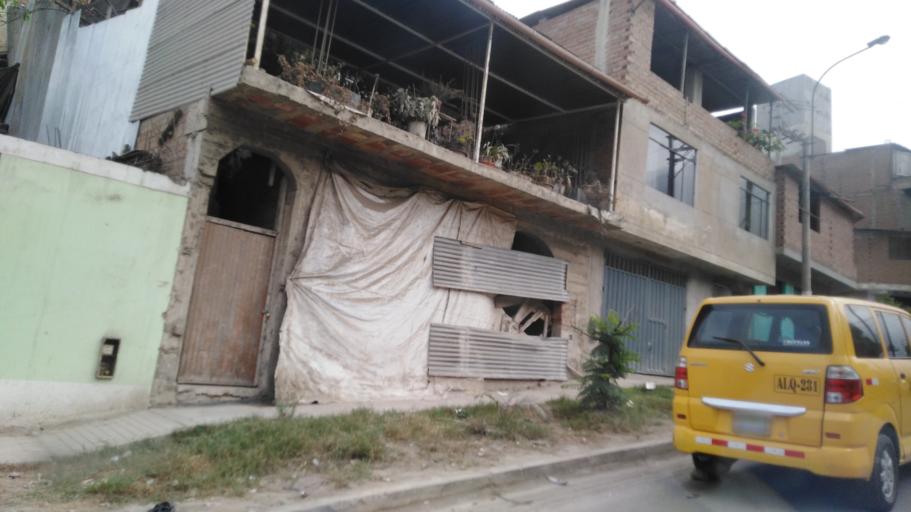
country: PE
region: Lima
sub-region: Lima
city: La Molina
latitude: -12.1472
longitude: -76.9311
